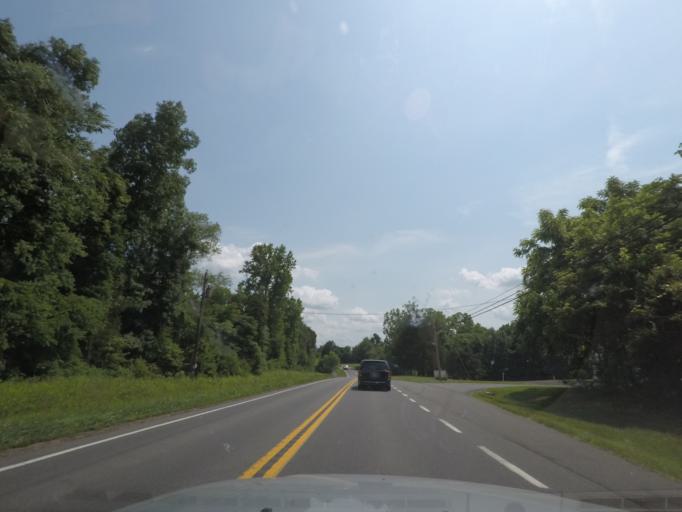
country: US
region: Virginia
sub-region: Orange County
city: Orange
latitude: 38.2933
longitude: -78.1381
